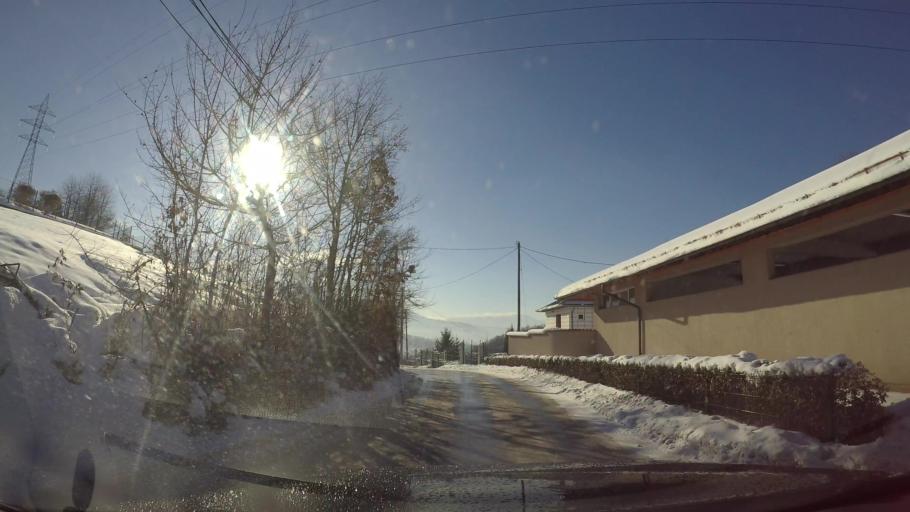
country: BA
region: Federation of Bosnia and Herzegovina
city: Kobilja Glava
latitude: 43.8946
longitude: 18.4158
